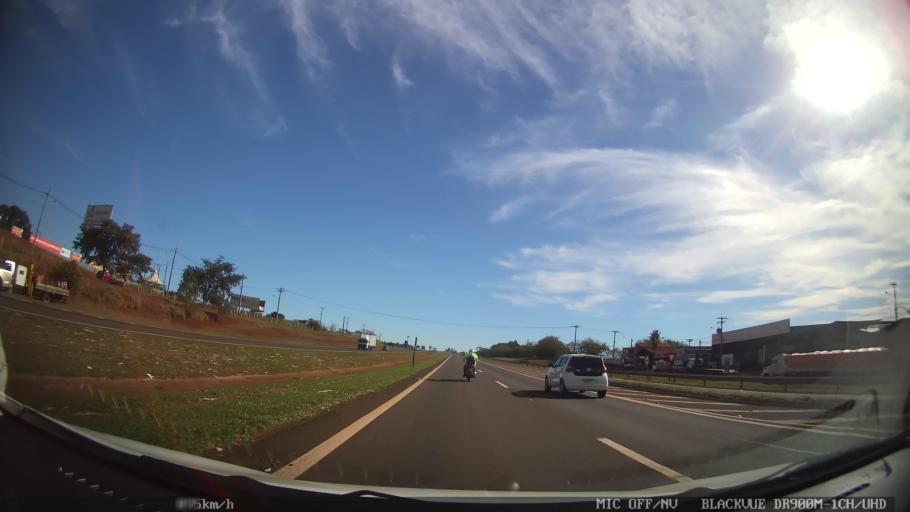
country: BR
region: Sao Paulo
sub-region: Araraquara
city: Araraquara
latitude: -21.8159
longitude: -48.1735
